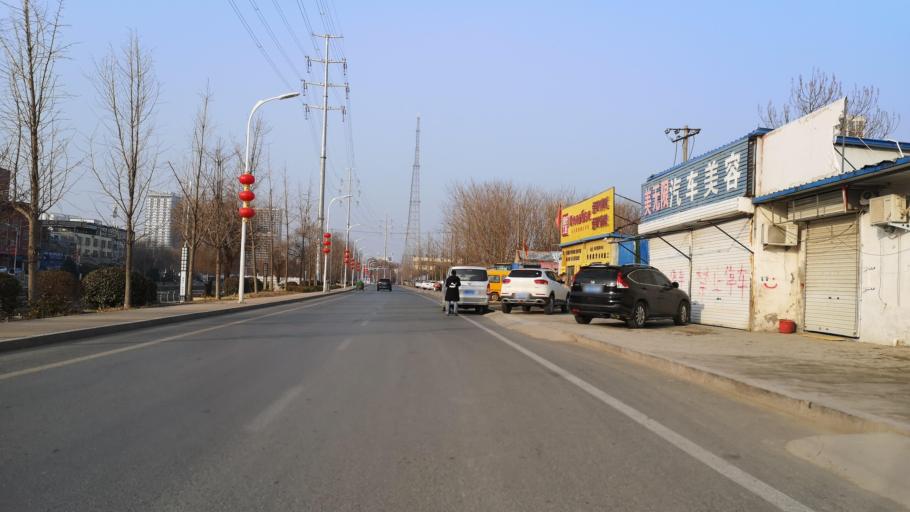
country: CN
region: Henan Sheng
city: Zhongyuanlu
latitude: 35.7732
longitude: 115.0486
